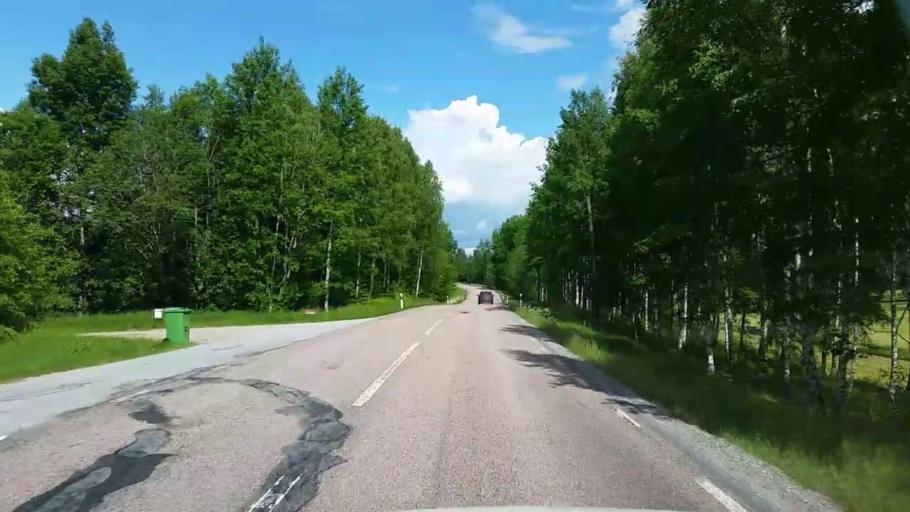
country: SE
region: Vaestmanland
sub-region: Fagersta Kommun
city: Fagersta
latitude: 59.9319
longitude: 15.8264
